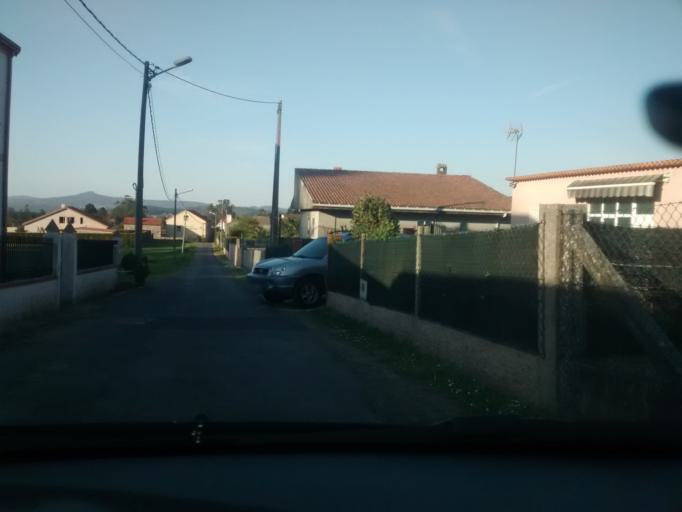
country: ES
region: Galicia
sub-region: Provincia de Pontevedra
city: A Estrada
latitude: 42.6950
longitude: -8.4826
